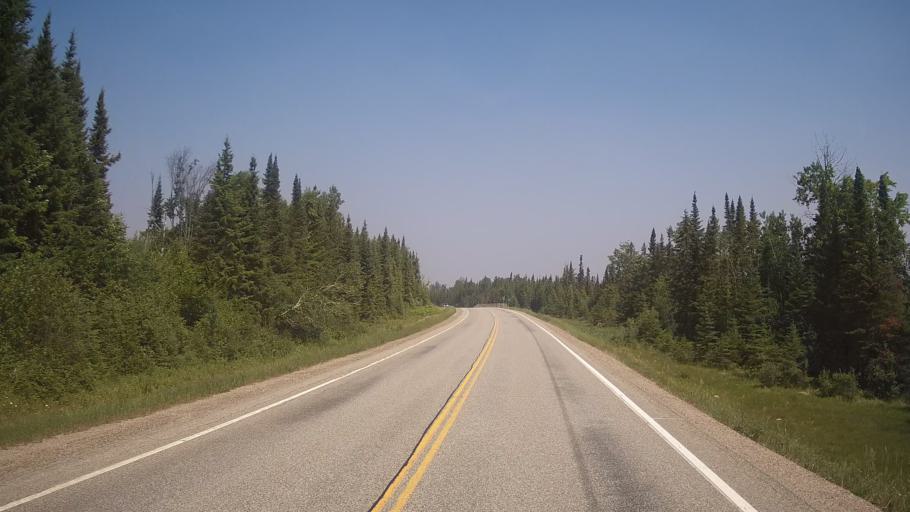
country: CA
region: Ontario
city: Timmins
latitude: 48.1712
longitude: -81.5825
